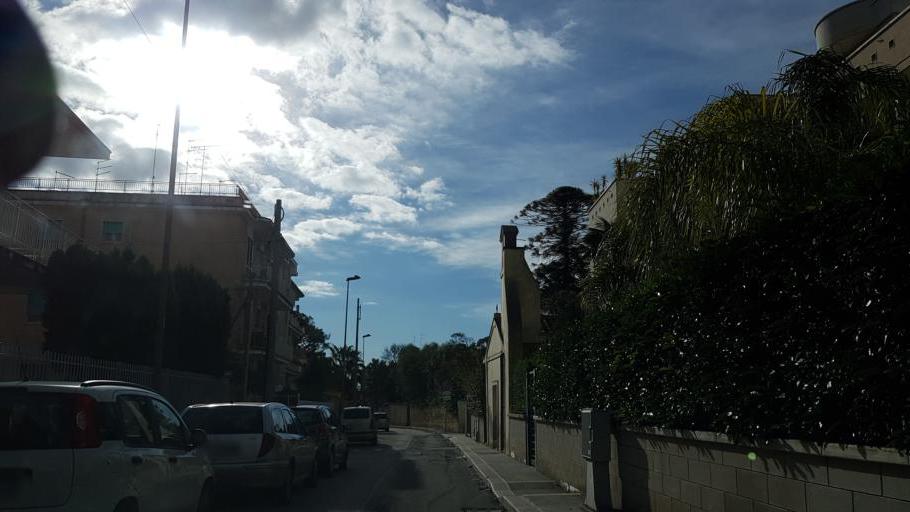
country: IT
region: Apulia
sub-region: Provincia di Brindisi
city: Brindisi
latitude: 40.6475
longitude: 17.9403
